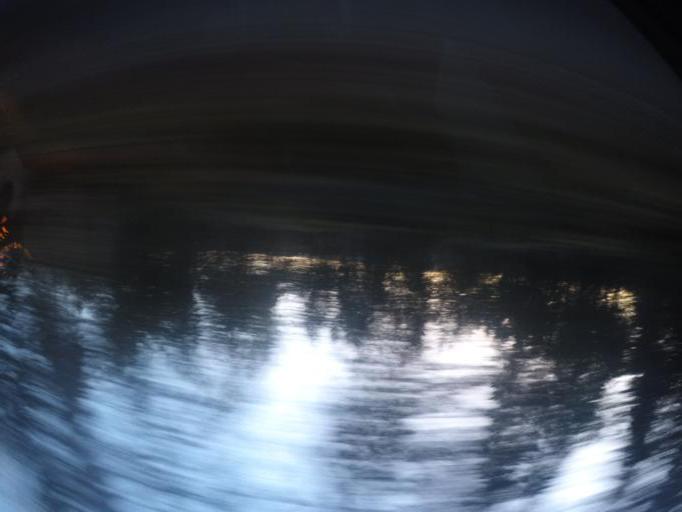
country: SE
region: OErebro
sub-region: Lindesbergs Kommun
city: Fellingsbro
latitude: 59.3407
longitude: 15.5377
